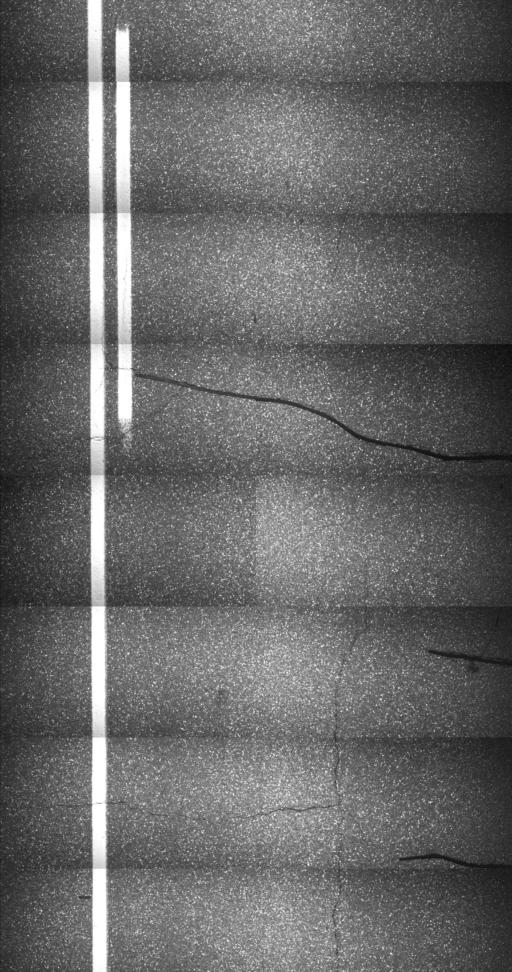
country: US
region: Vermont
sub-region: Orange County
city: Chelsea
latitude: 44.1324
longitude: -72.3143
